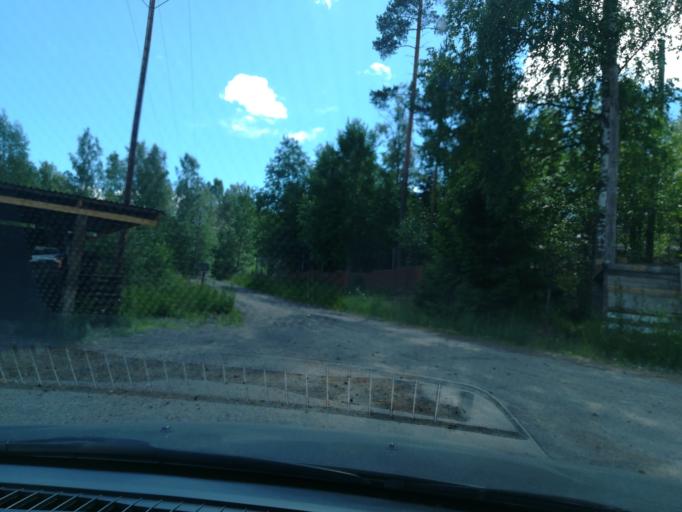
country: FI
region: Southern Savonia
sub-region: Mikkeli
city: Hirvensalmi
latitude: 61.6607
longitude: 27.0037
